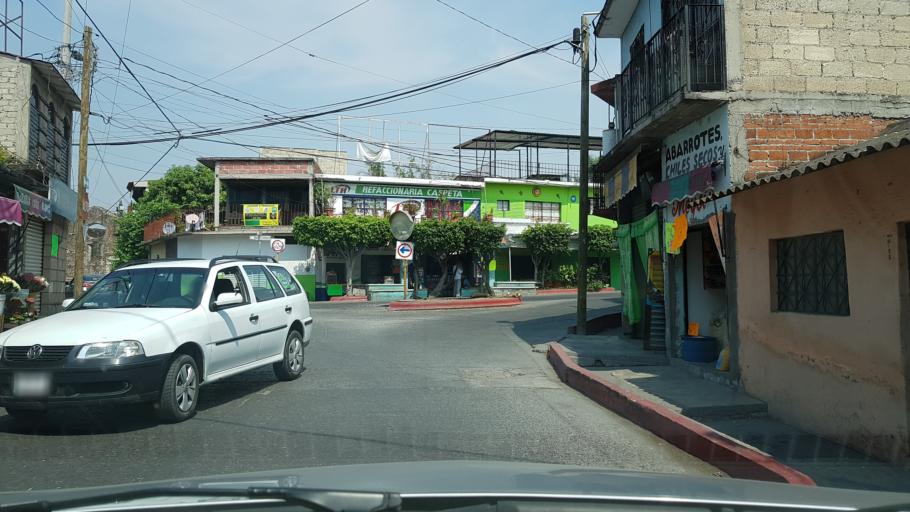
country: MX
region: Morelos
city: Emiliano Zapata
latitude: 18.8379
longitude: -99.1834
